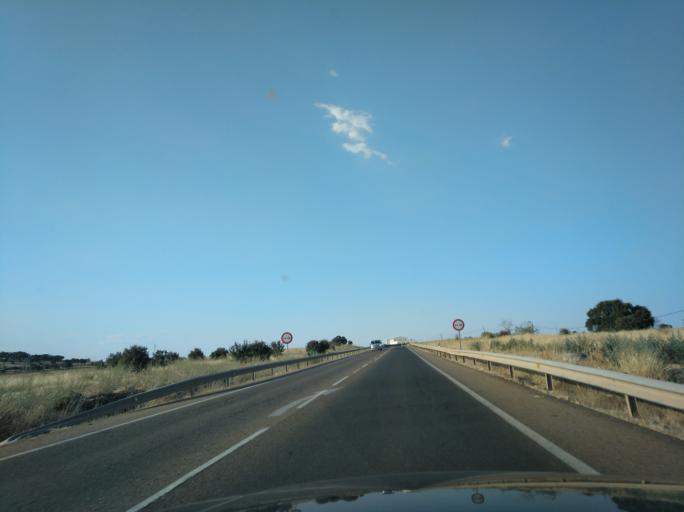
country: ES
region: Extremadura
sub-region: Provincia de Badajoz
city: Olivenza
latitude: 38.7025
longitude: -7.0879
